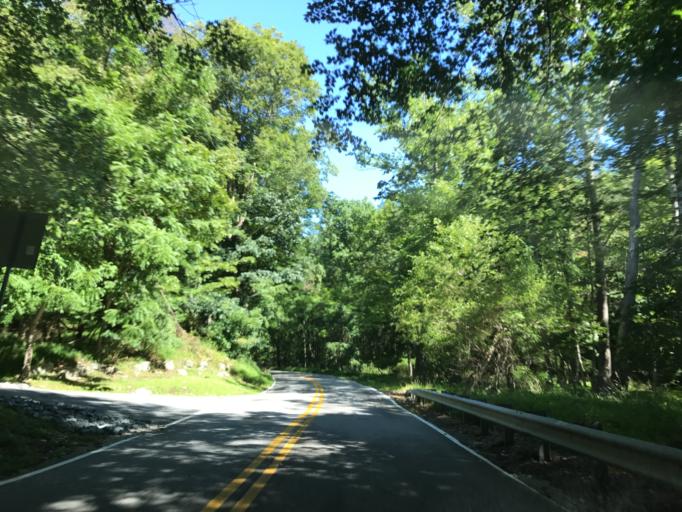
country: US
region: Maryland
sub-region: Howard County
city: Ilchester
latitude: 39.2576
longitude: -76.7652
